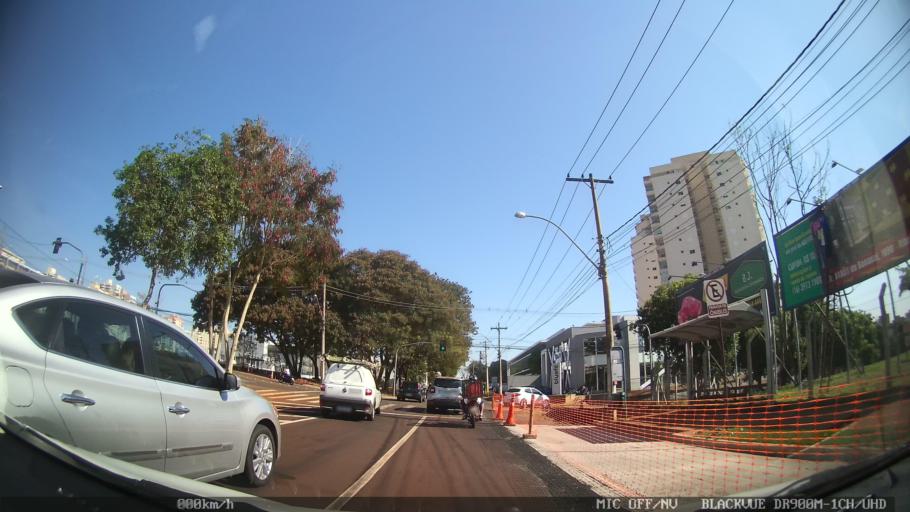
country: BR
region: Sao Paulo
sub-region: Ribeirao Preto
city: Ribeirao Preto
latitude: -21.2170
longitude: -47.8180
